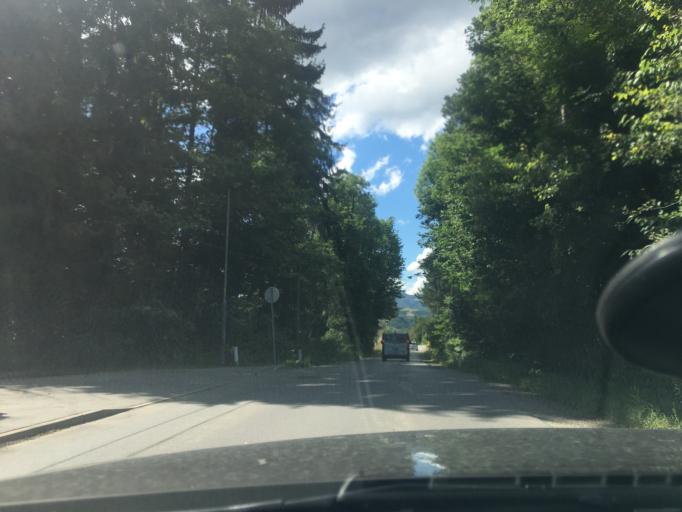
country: SI
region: Maribor
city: Pekre
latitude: 46.5442
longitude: 15.6019
